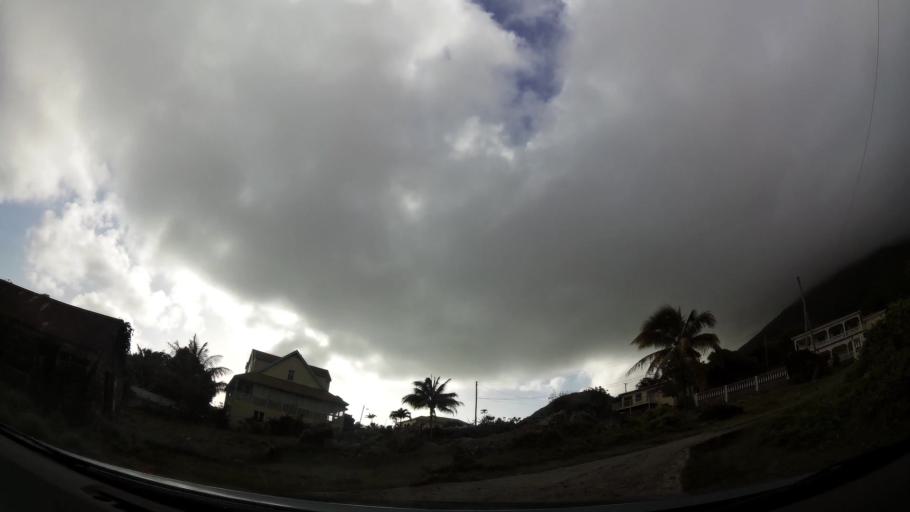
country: KN
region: Saint George Gingerland
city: Market Shop
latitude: 17.1390
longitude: -62.5738
